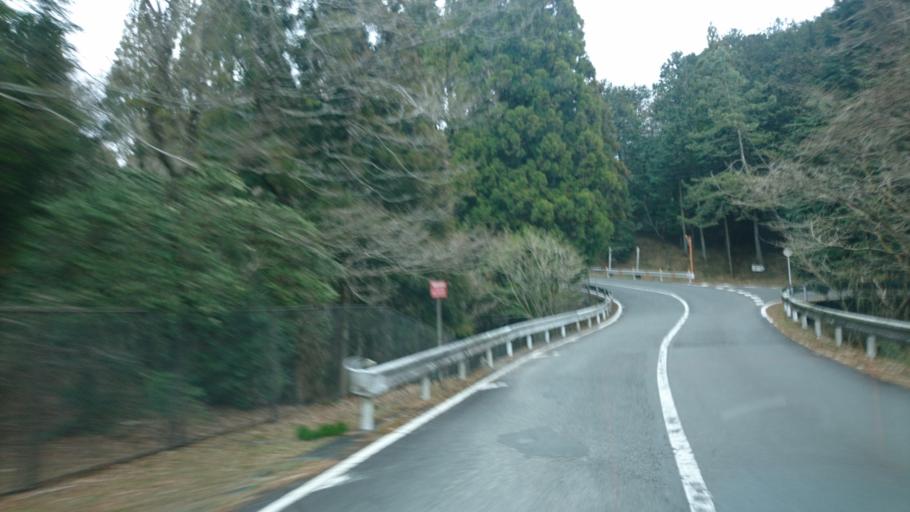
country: JP
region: Shizuoka
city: Fujinomiya
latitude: 35.3364
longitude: 138.5685
